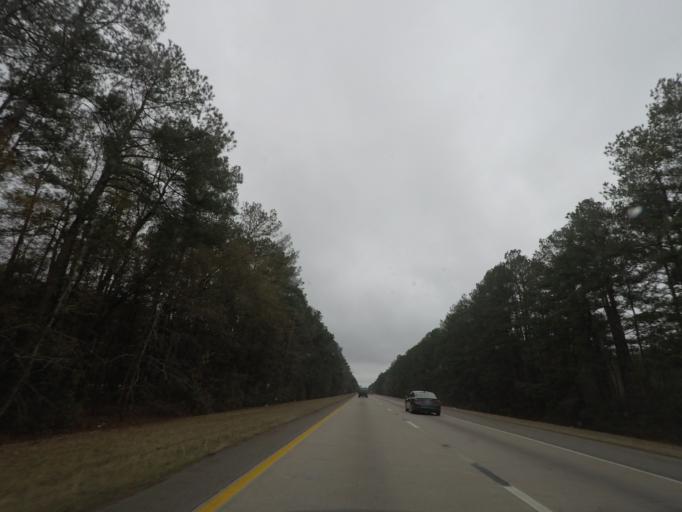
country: US
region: South Carolina
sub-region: Colleton County
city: Walterboro
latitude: 32.9753
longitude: -80.6756
